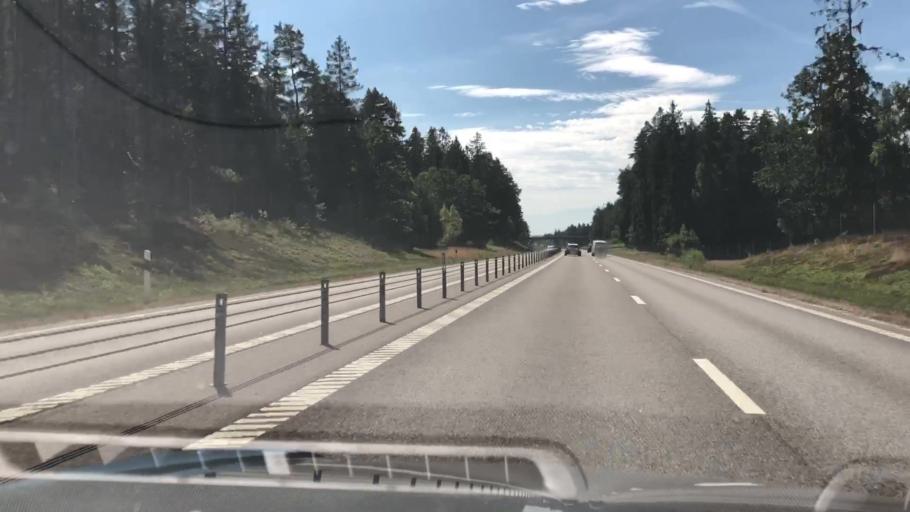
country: SE
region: Kalmar
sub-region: Kalmar Kommun
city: Ljungbyholm
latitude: 56.5381
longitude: 16.0836
